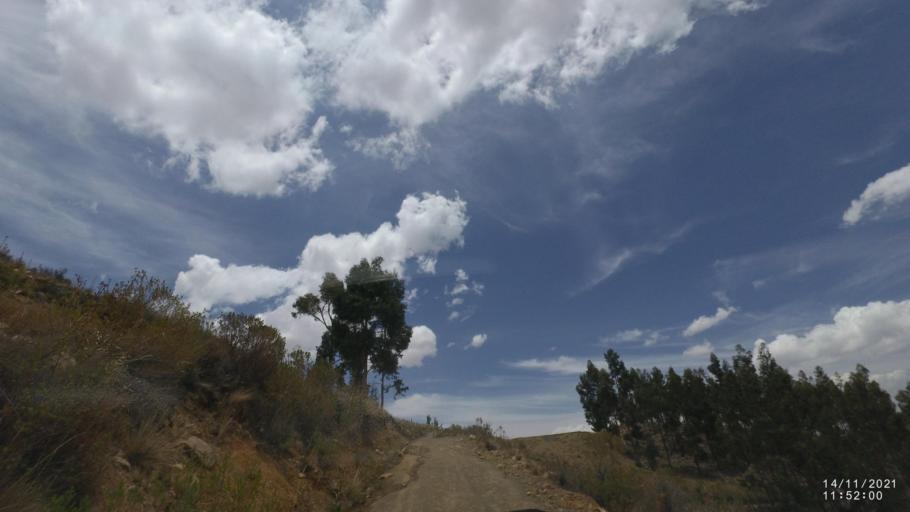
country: BO
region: Cochabamba
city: Colomi
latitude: -17.3619
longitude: -65.9828
